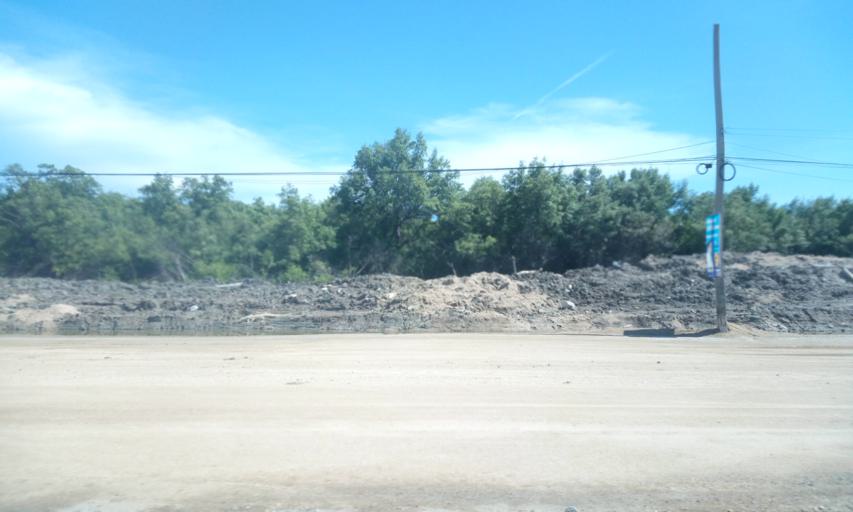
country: TH
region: Samut Prakan
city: Bang Bo District
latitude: 13.5023
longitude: 100.7617
